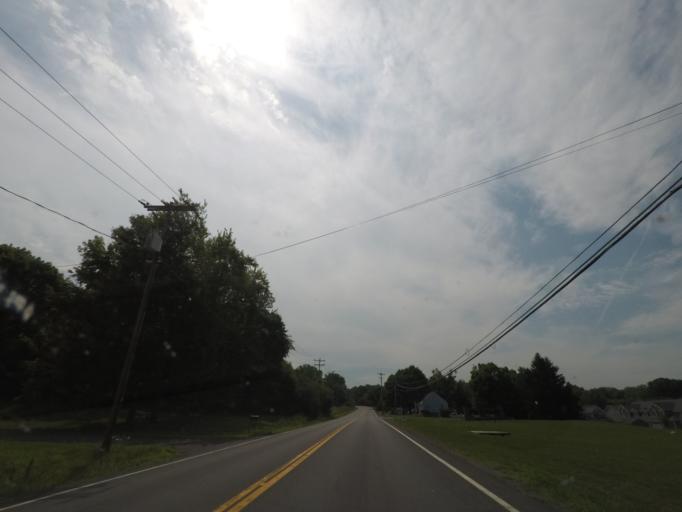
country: US
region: New York
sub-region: Saratoga County
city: Waterford
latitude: 42.7813
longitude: -73.6491
